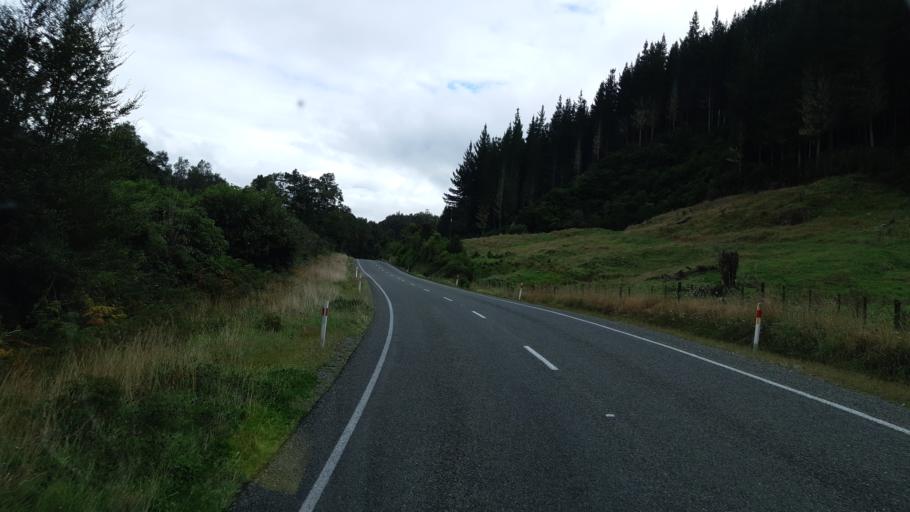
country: NZ
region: West Coast
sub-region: Buller District
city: Westport
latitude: -41.8278
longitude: 172.2399
